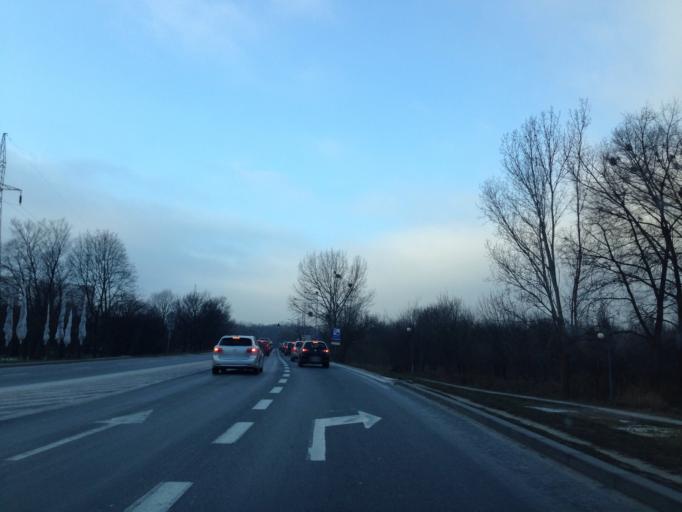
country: PL
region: Greater Poland Voivodeship
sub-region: Poznan
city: Poznan
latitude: 52.4404
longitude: 16.9492
